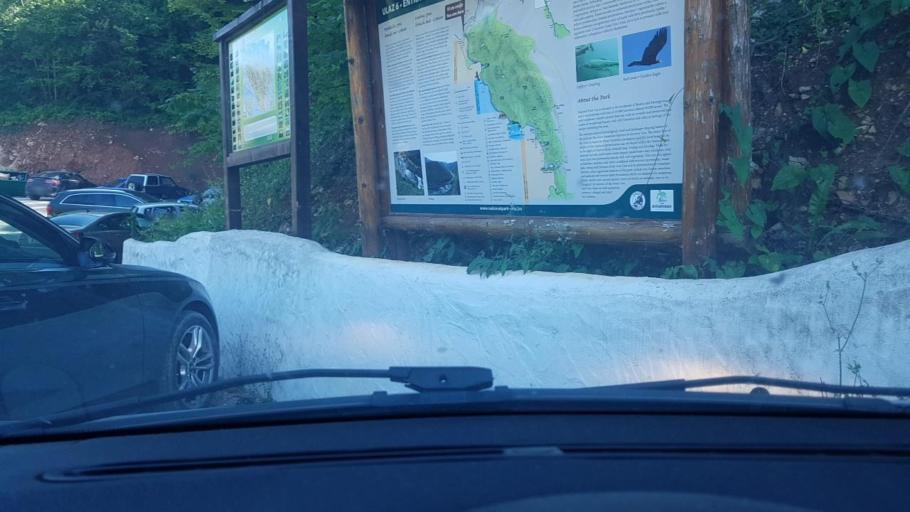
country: BA
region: Federation of Bosnia and Herzegovina
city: Bihac
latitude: 44.7339
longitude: 15.9257
